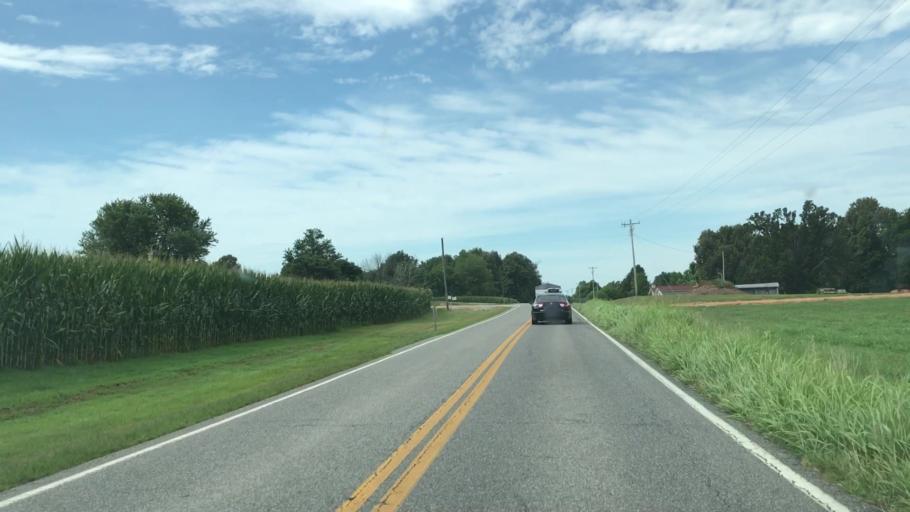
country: US
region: Kentucky
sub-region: Graves County
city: Mayfield
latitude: 36.8500
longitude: -88.5740
